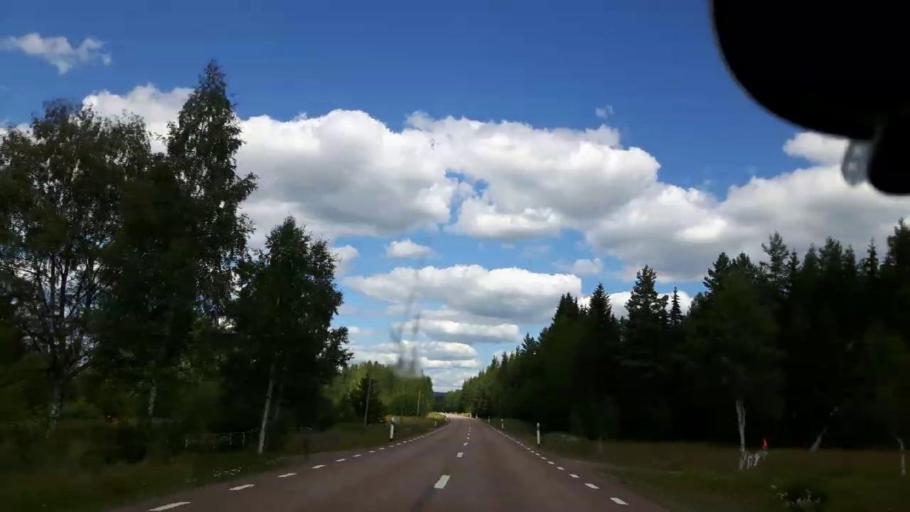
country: SE
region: Jaemtland
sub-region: Ragunda Kommun
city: Hammarstrand
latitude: 62.9064
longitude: 16.7015
